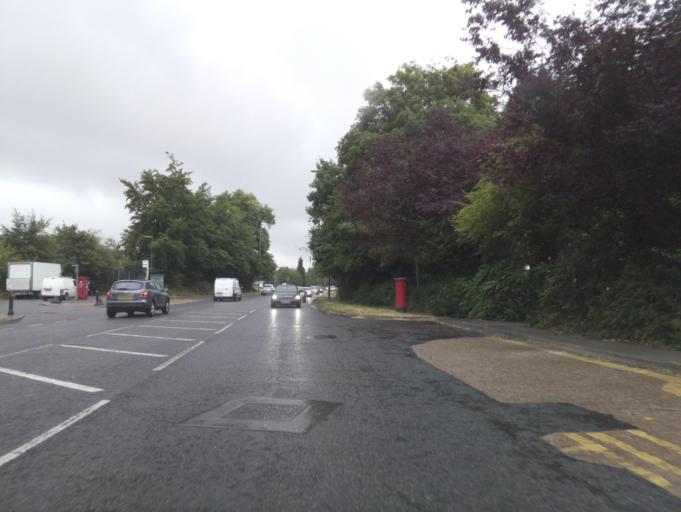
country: GB
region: England
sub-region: Surrey
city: Salfords
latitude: 51.1983
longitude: -0.1657
